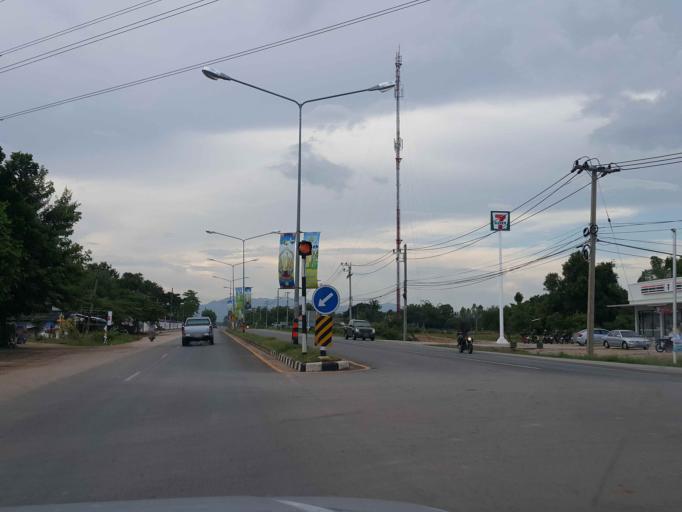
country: TH
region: Lampang
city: Hang Chat
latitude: 18.2793
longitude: 99.3825
